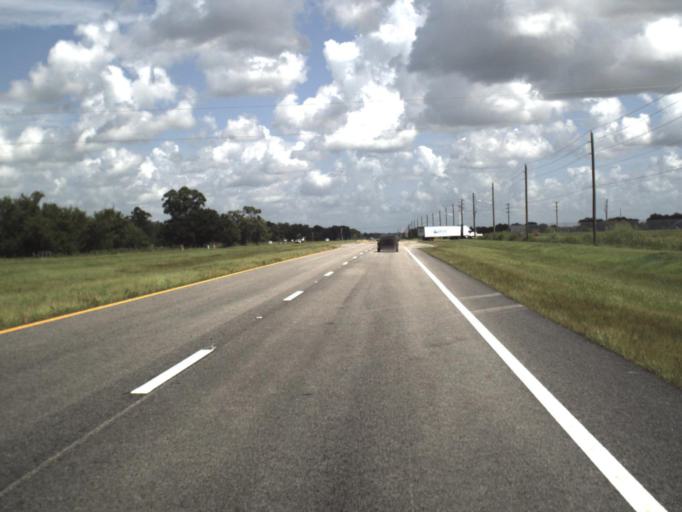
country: US
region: Florida
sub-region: Charlotte County
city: Harbour Heights
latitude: 27.0425
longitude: -81.9583
